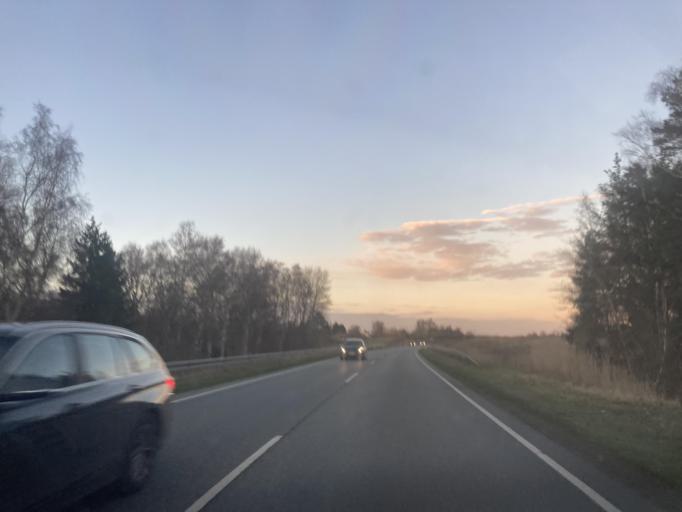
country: DK
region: Capital Region
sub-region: Gribskov Kommune
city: Graested
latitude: 56.0659
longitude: 12.2732
